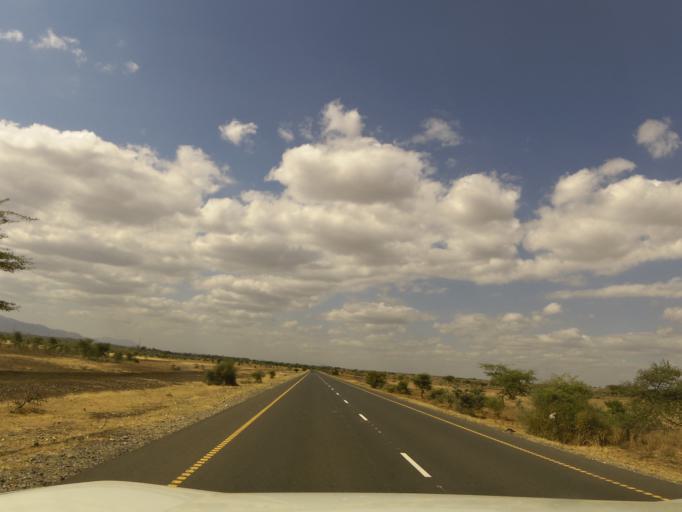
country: TZ
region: Arusha
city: Mto wa Mbu
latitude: -3.5856
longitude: 36.0648
